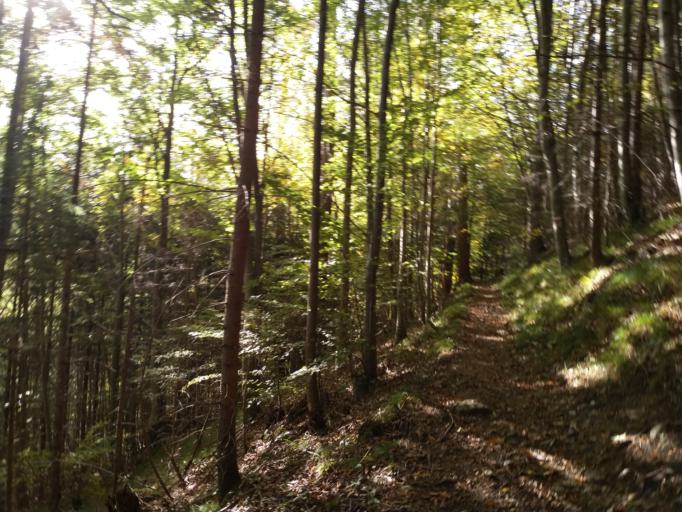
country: AT
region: Tyrol
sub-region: Politischer Bezirk Reutte
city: Vils
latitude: 47.5628
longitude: 10.6514
